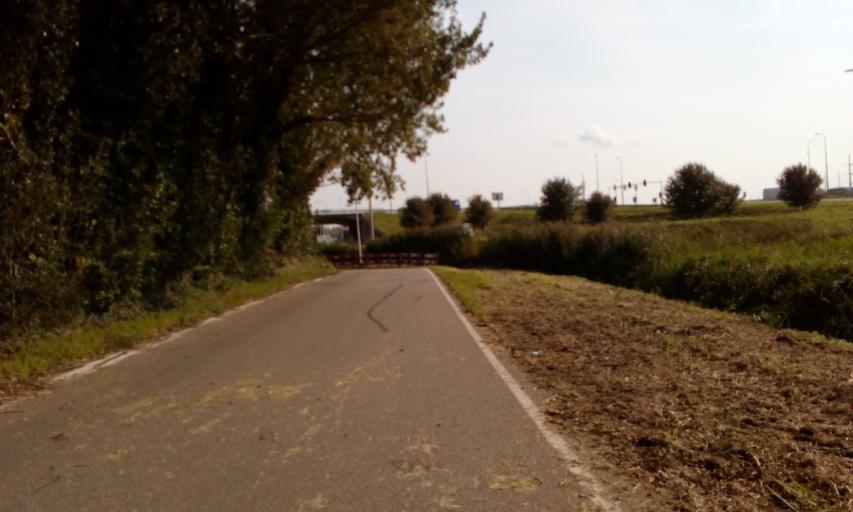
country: NL
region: South Holland
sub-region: Gemeente Rijswijk
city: Rijswijk
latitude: 52.0150
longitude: 4.3102
